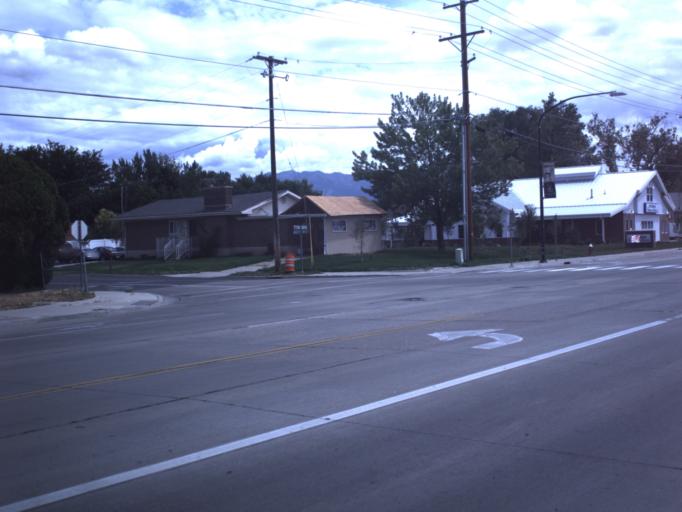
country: US
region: Utah
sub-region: Davis County
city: Syracuse
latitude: 41.0890
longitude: -112.0542
